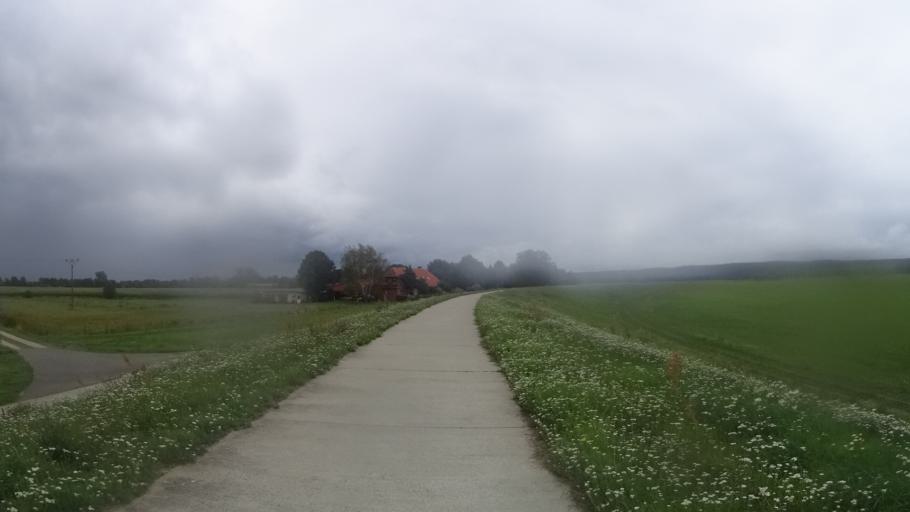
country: DE
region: Lower Saxony
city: Tosterglope
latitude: 53.2797
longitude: 10.8252
